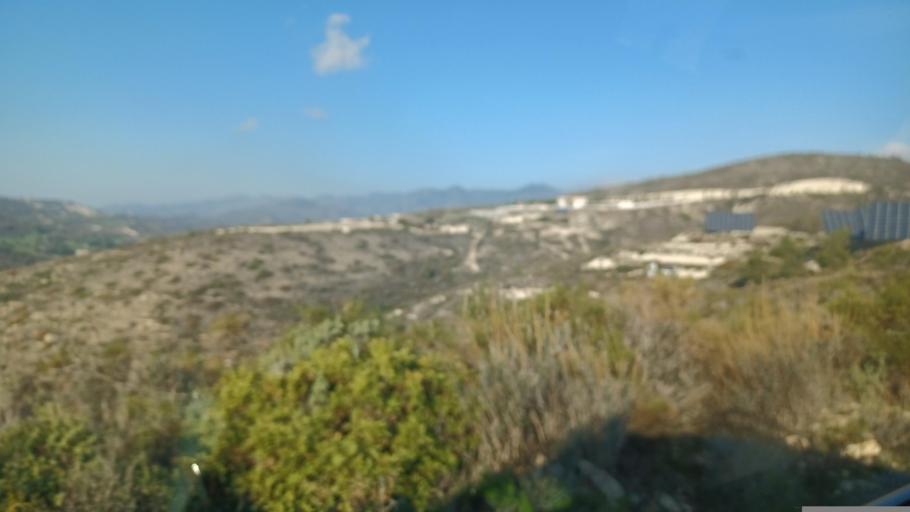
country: CY
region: Larnaka
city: Kofinou
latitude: 34.8388
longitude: 33.3024
